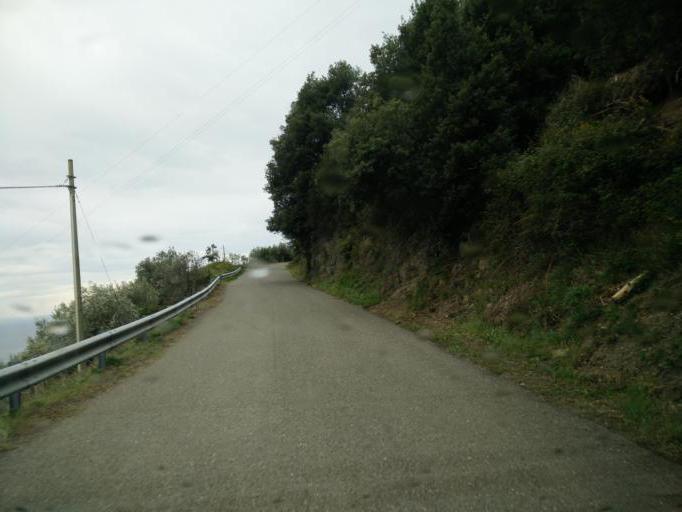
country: IT
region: Liguria
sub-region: Provincia di La Spezia
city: Vernazza
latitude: 44.1428
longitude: 9.6863
